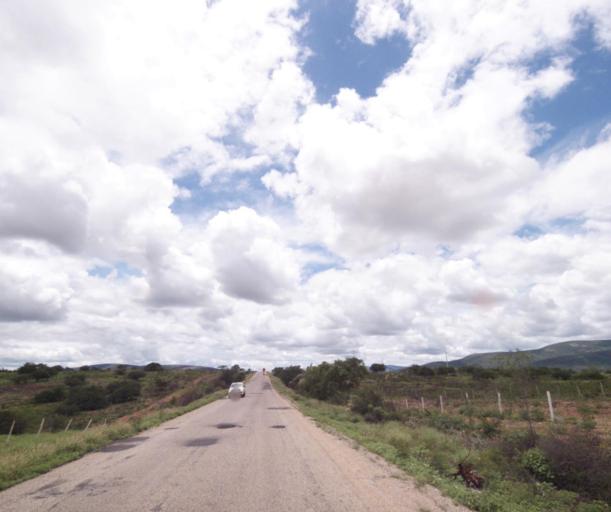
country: BR
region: Bahia
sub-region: Brumado
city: Brumado
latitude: -14.1572
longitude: -41.5212
